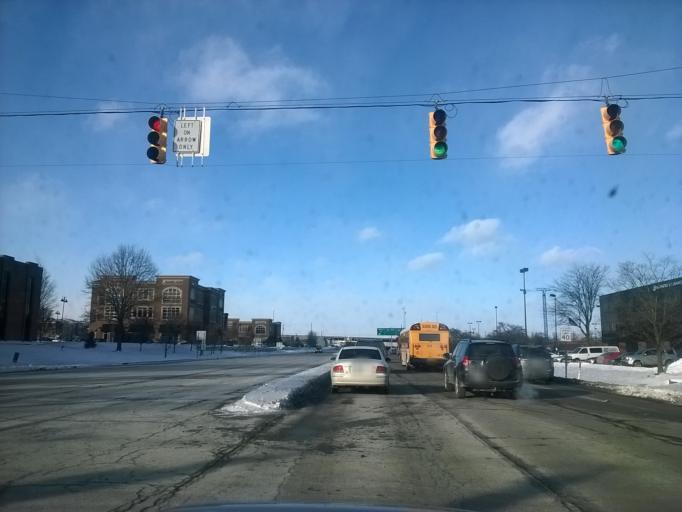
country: US
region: Indiana
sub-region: Marion County
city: Meridian Hills
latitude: 39.9234
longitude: -86.1578
